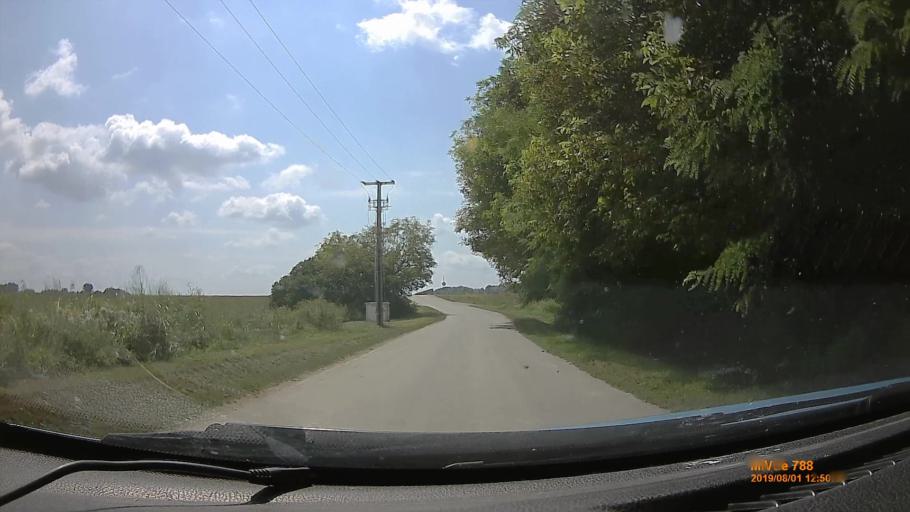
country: HR
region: Osjecko-Baranjska
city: Viljevo
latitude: 45.8078
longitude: 18.1030
